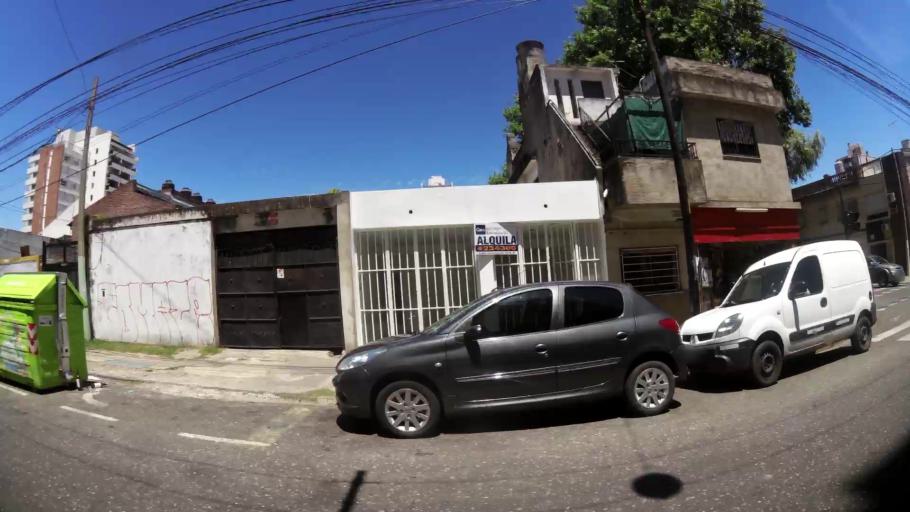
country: AR
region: Santa Fe
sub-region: Departamento de Rosario
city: Rosario
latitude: -32.9464
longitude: -60.6680
